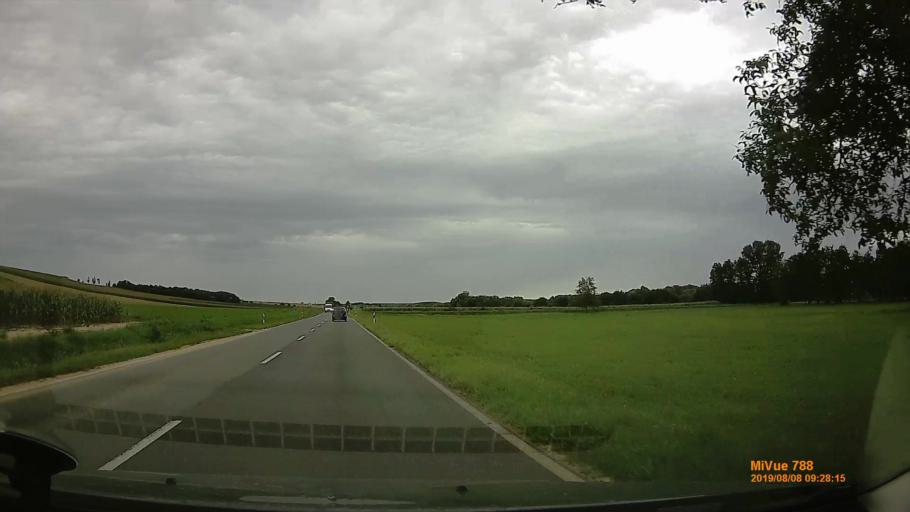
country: HU
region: Vas
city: Vasvar
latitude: 46.9598
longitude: 16.8452
